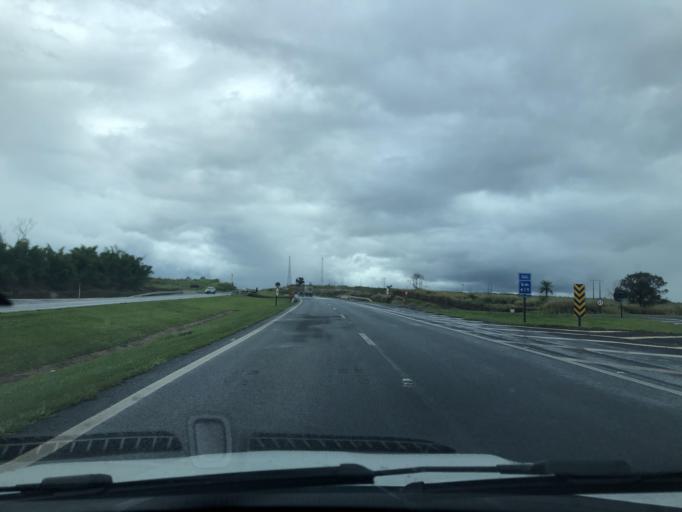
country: BR
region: Sao Paulo
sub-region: Ituverava
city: Ituverava
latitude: -20.2587
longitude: -47.8002
